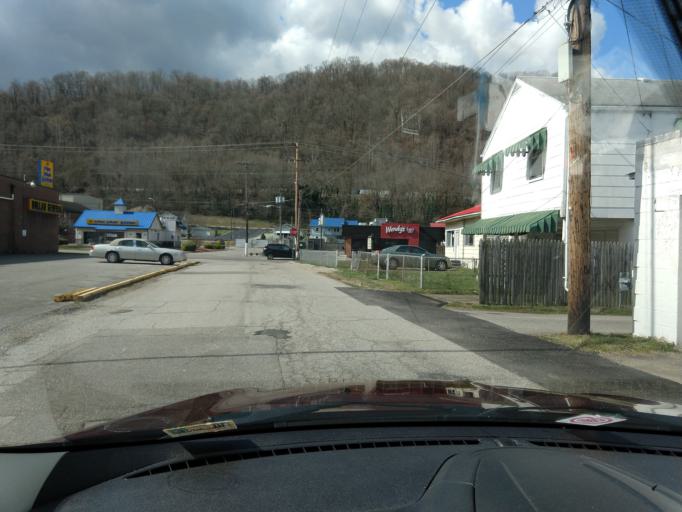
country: US
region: West Virginia
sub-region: Kanawha County
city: Marmet
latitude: 38.2476
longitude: -81.5680
